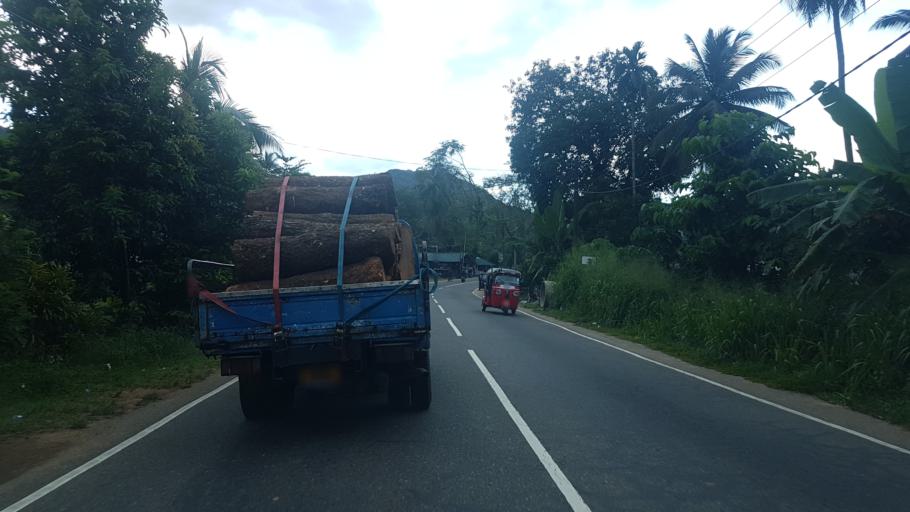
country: LK
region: Western
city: Hanwella Ihala
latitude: 7.0218
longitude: 80.2623
